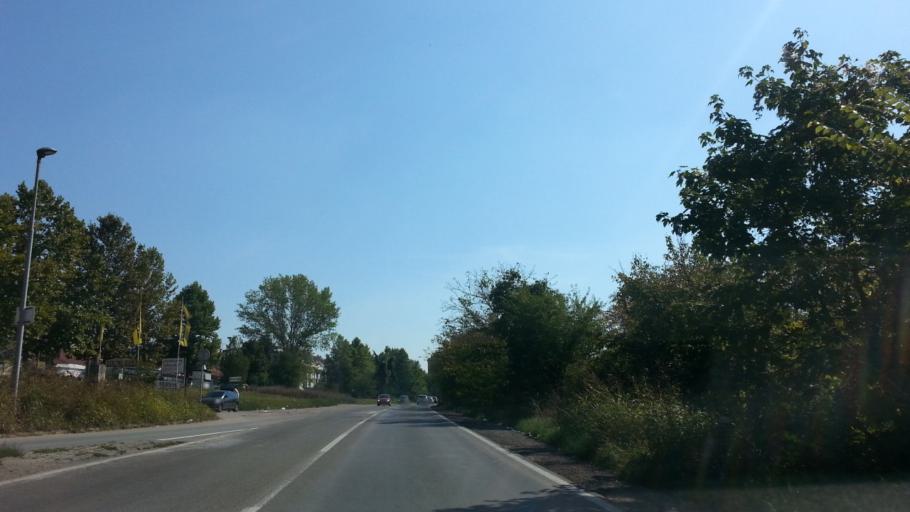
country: RS
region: Central Serbia
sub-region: Belgrade
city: Rakovica
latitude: 44.7393
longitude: 20.4157
